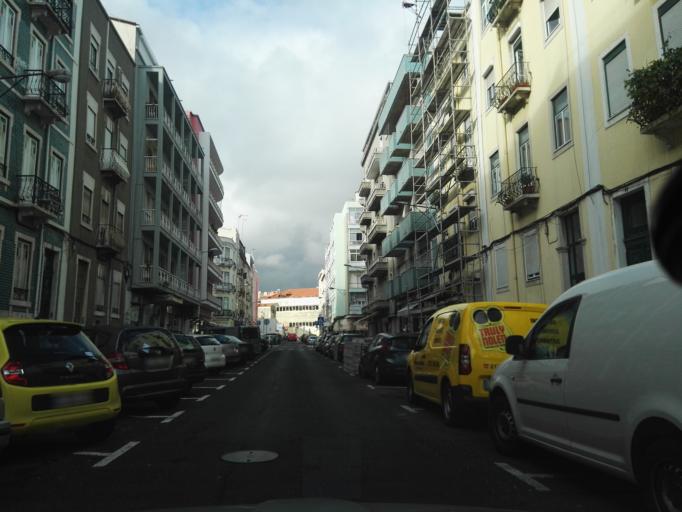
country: PT
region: Lisbon
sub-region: Lisbon
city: Lisbon
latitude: 38.7323
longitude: -9.1352
